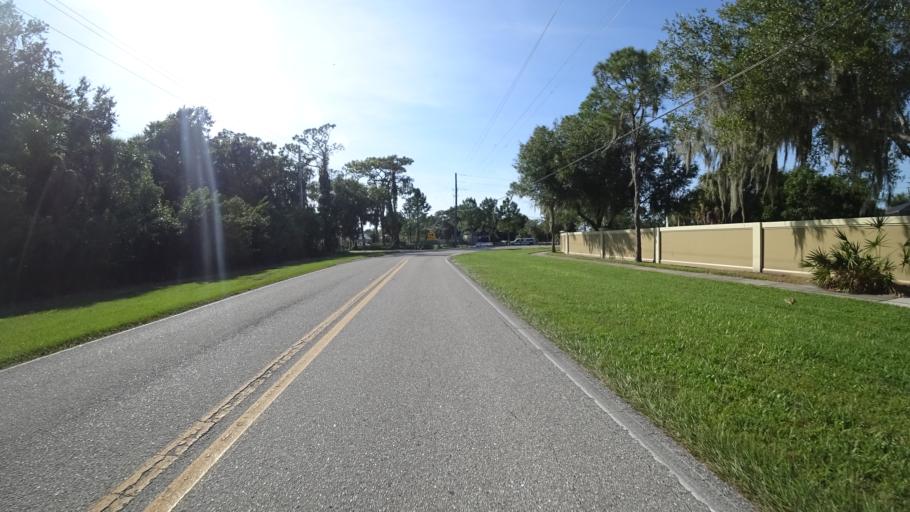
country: US
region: Florida
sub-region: Sarasota County
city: Desoto Lakes
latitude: 27.4325
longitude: -82.4804
